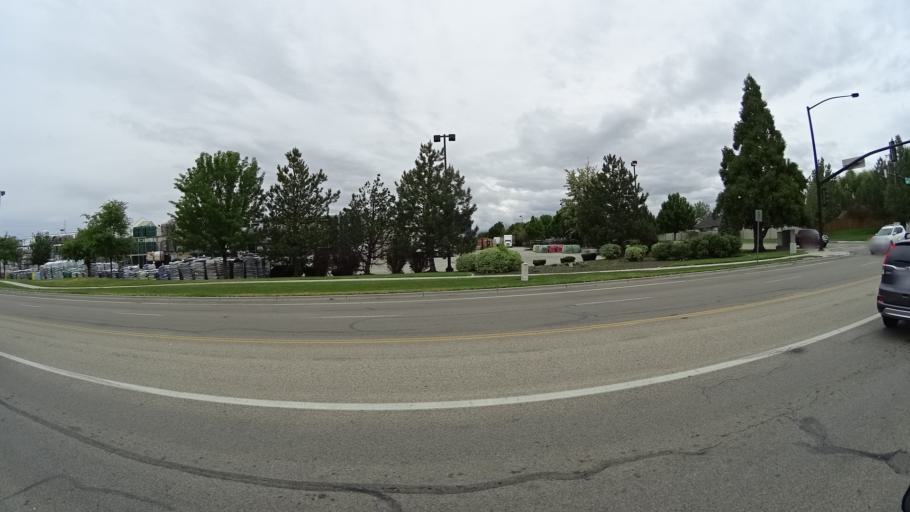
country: US
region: Idaho
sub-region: Ada County
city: Meridian
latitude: 43.6338
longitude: -116.3504
